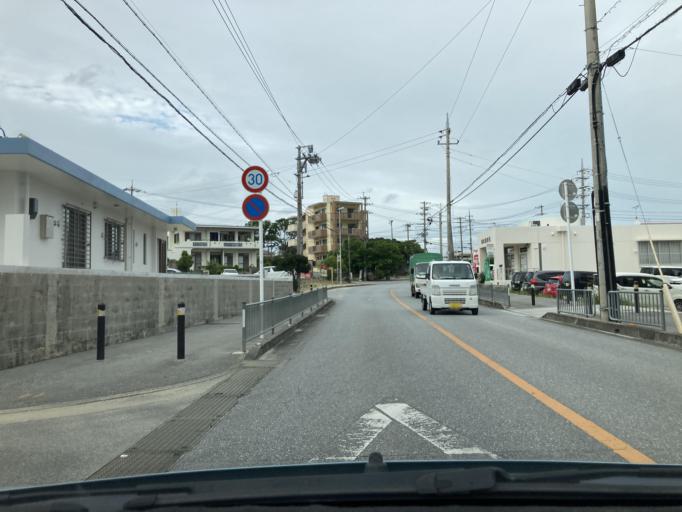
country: JP
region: Okinawa
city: Itoman
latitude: 26.1464
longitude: 127.6920
